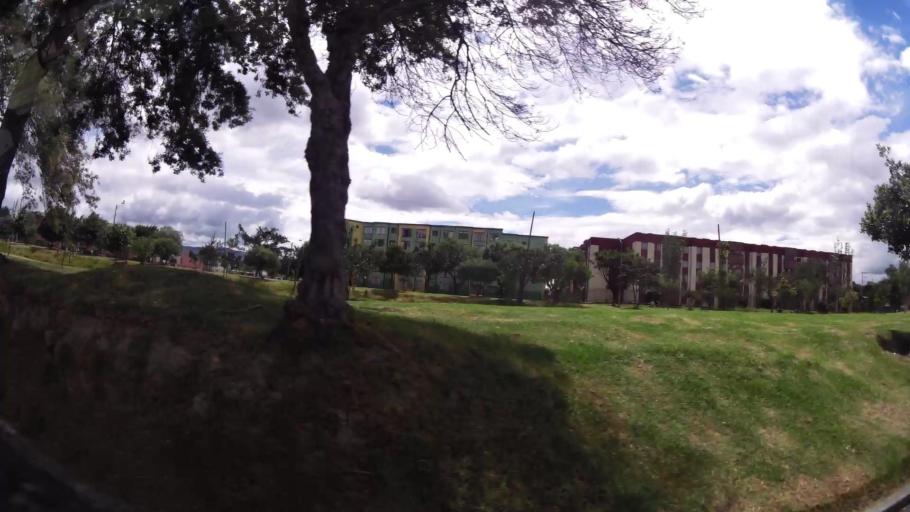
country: CO
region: Bogota D.C.
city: Bogota
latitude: 4.6144
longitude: -74.1237
